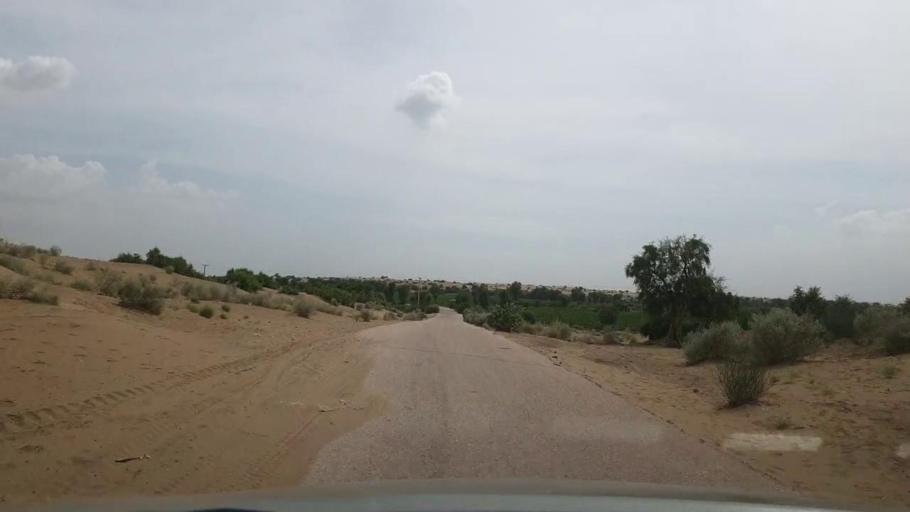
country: PK
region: Sindh
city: Kot Diji
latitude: 27.1655
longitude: 69.0362
